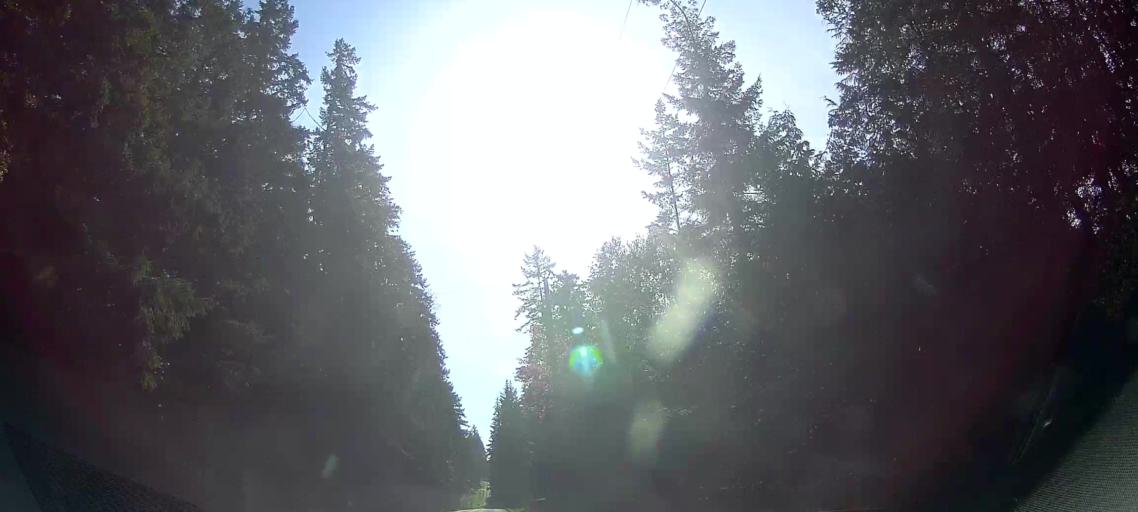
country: US
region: Washington
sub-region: Island County
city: Camano
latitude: 48.2183
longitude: -122.4560
